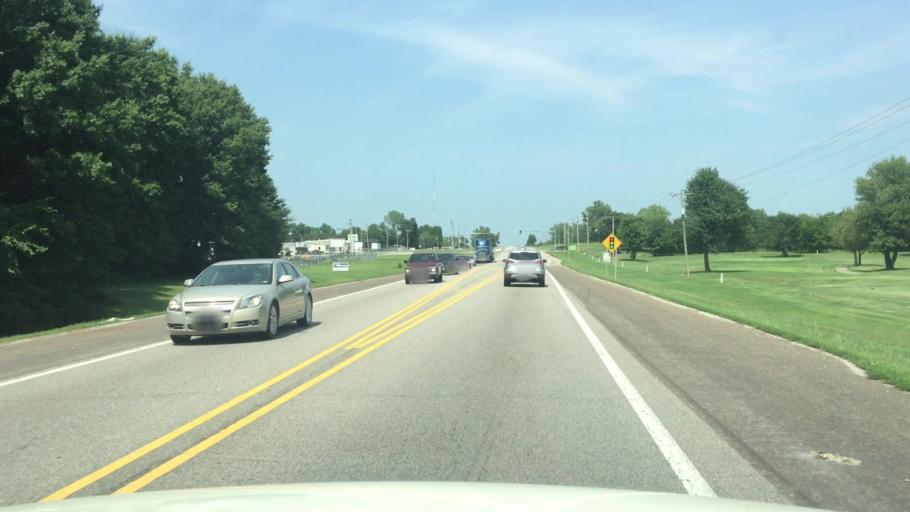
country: US
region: Kansas
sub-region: Crawford County
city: Pittsburg
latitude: 37.4231
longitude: -94.7177
